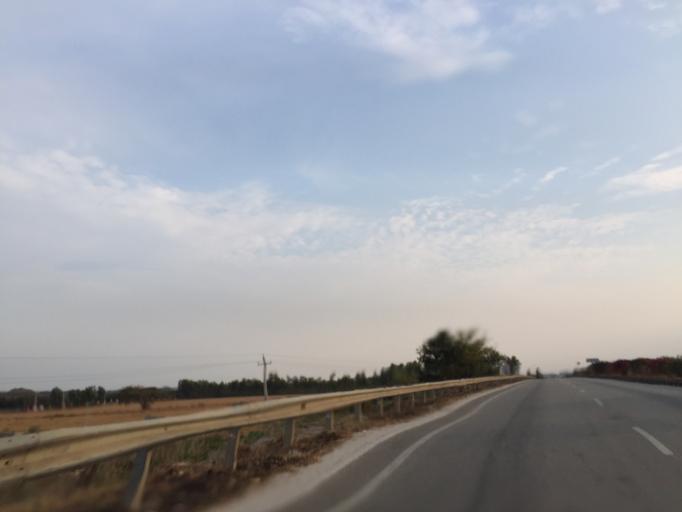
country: IN
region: Karnataka
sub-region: Chikkaballapur
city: Chik Ballapur
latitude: 13.4070
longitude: 77.7430
